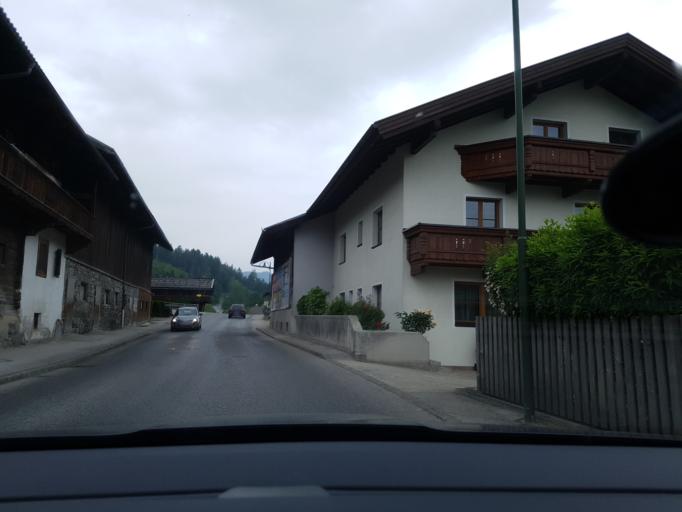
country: AT
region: Tyrol
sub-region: Politischer Bezirk Schwaz
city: Fugen
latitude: 47.3494
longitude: 11.8501
